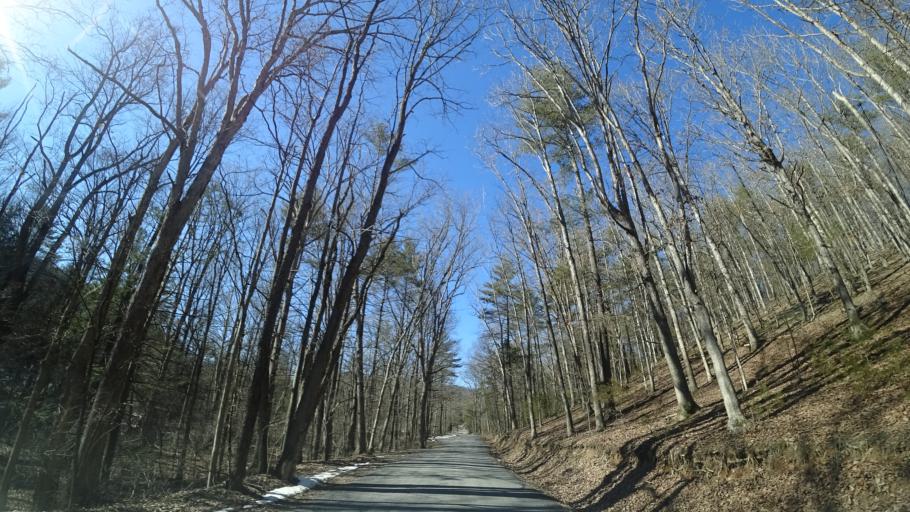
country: US
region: West Virginia
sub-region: Hardy County
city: Moorefield
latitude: 39.0210
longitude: -78.7675
